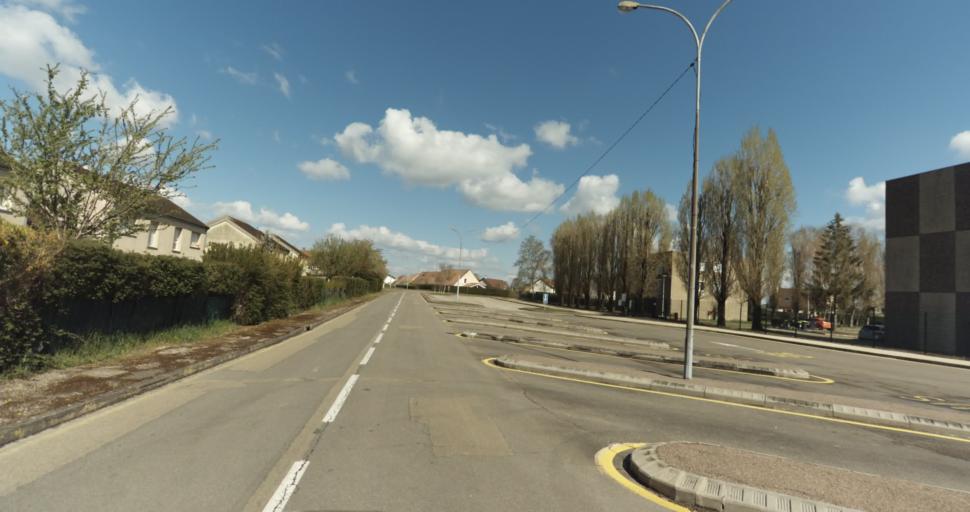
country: FR
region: Bourgogne
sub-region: Departement de la Cote-d'Or
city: Auxonne
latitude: 47.1987
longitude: 5.3987
